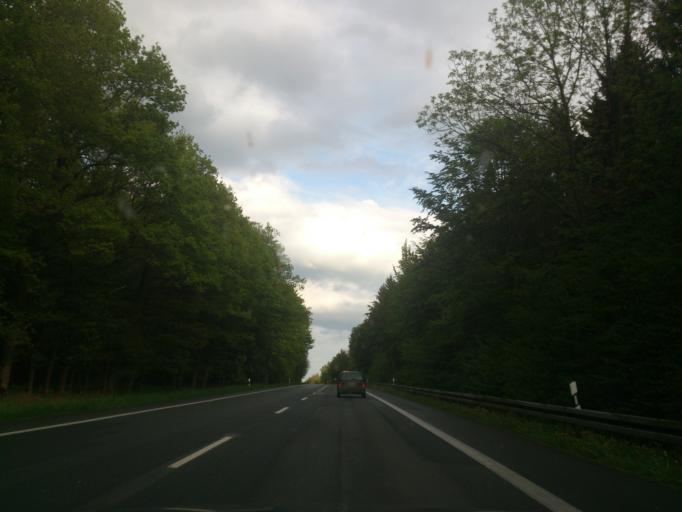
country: DE
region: North Rhine-Westphalia
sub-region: Regierungsbezirk Detmold
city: Bad Driburg
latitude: 51.6904
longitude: 8.9673
